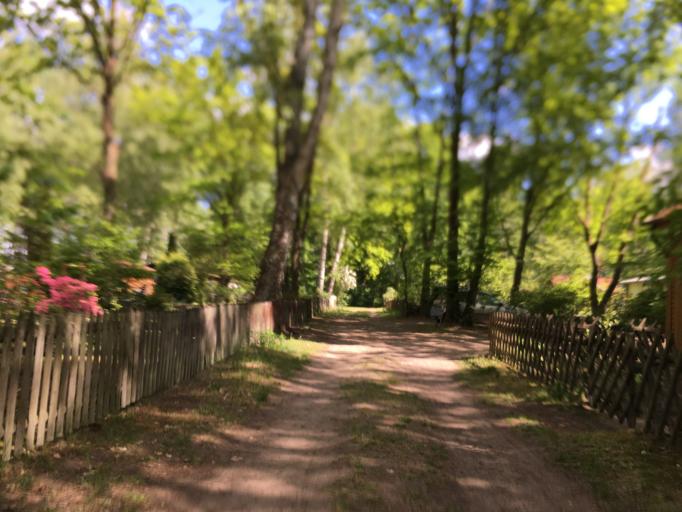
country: DE
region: Berlin
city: Blankenfelde
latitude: 52.6511
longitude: 13.3794
